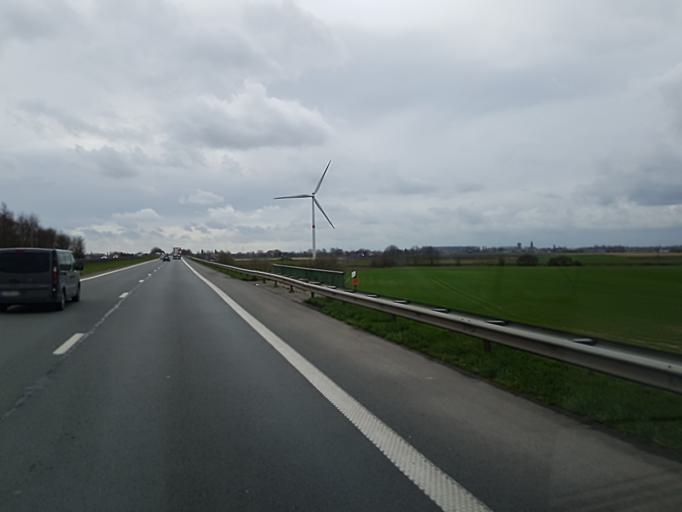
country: BE
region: Wallonia
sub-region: Province du Hainaut
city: Estaimpuis
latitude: 50.6811
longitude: 3.2912
